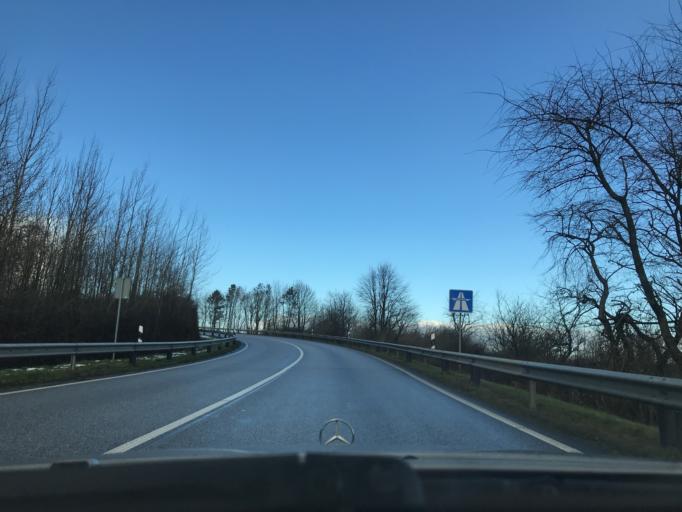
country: DE
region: Schleswig-Holstein
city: Handewitt
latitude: 54.7732
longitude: 9.3482
